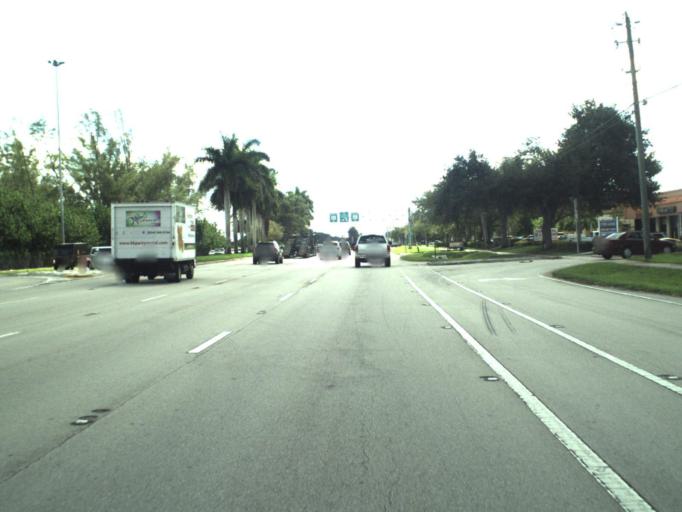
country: US
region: Florida
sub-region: Broward County
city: Sunshine Ranches
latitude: 26.0076
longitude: -80.3180
